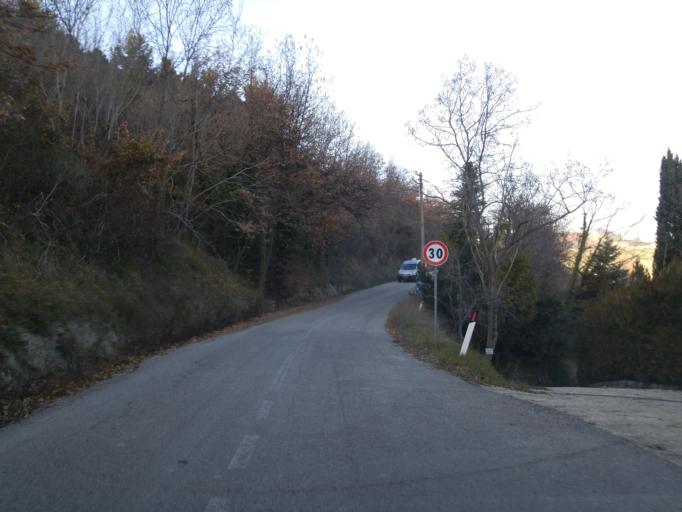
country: IT
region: The Marches
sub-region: Provincia di Pesaro e Urbino
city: Montefelcino
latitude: 43.7656
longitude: 12.8291
